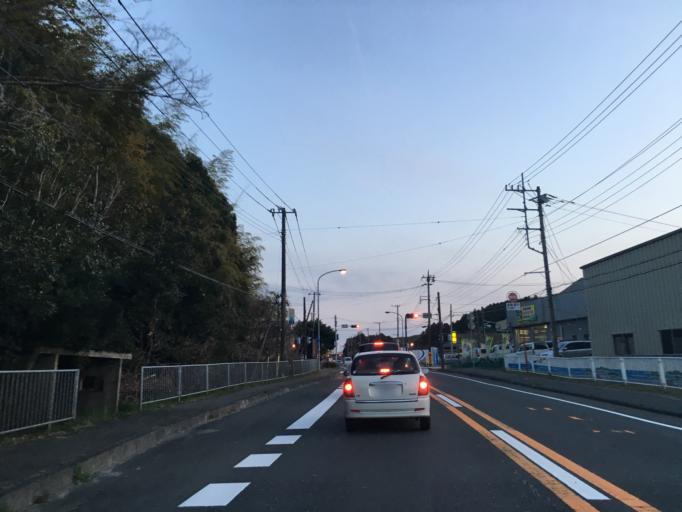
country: JP
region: Ibaraki
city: Takahagi
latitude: 36.7399
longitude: 140.7249
